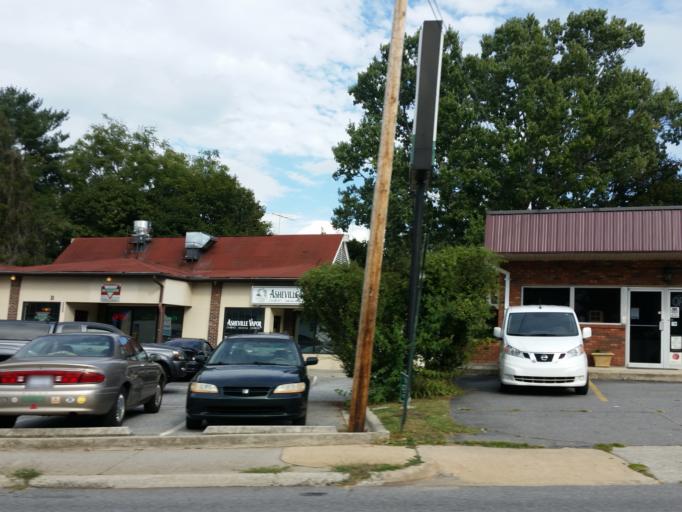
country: US
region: North Carolina
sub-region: Buncombe County
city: Asheville
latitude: 35.6104
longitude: -82.5547
